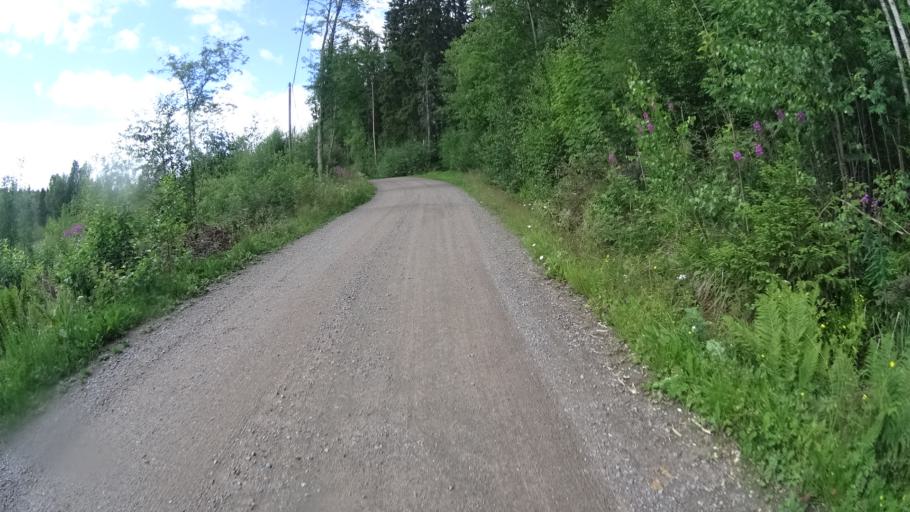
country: FI
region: Uusimaa
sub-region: Helsinki
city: Karkkila
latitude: 60.5959
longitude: 24.2200
